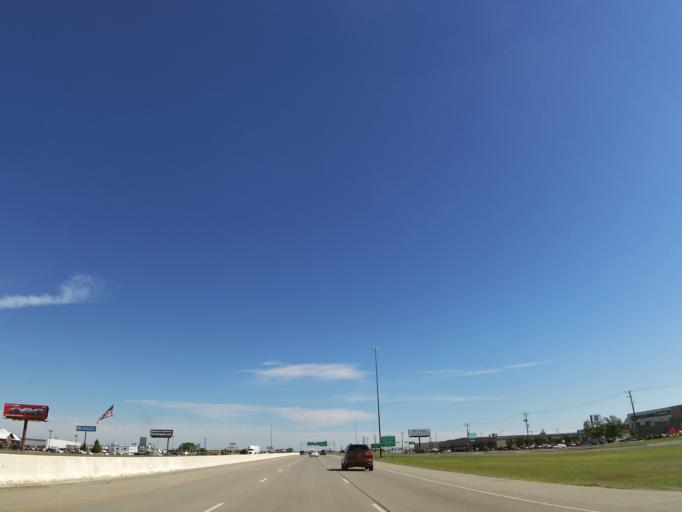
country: US
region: North Dakota
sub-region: Cass County
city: Fargo
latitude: 46.8694
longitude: -96.8416
